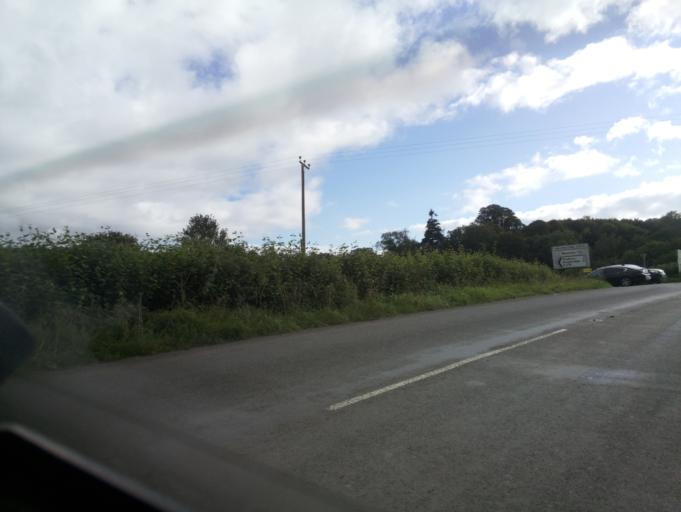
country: GB
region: England
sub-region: Devon
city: Ivybridge
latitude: 50.3533
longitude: -3.9273
